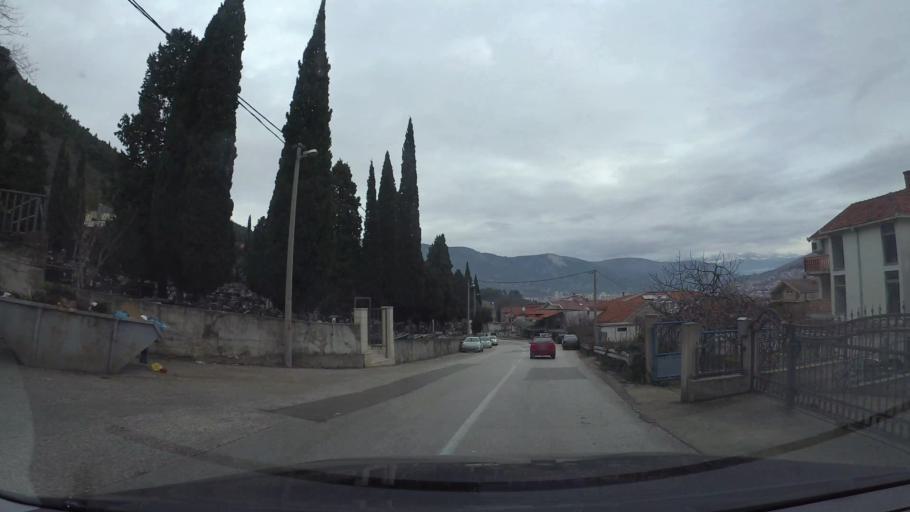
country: BA
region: Federation of Bosnia and Herzegovina
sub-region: Hercegovacko-Bosanski Kanton
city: Mostar
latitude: 43.3322
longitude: 17.7960
